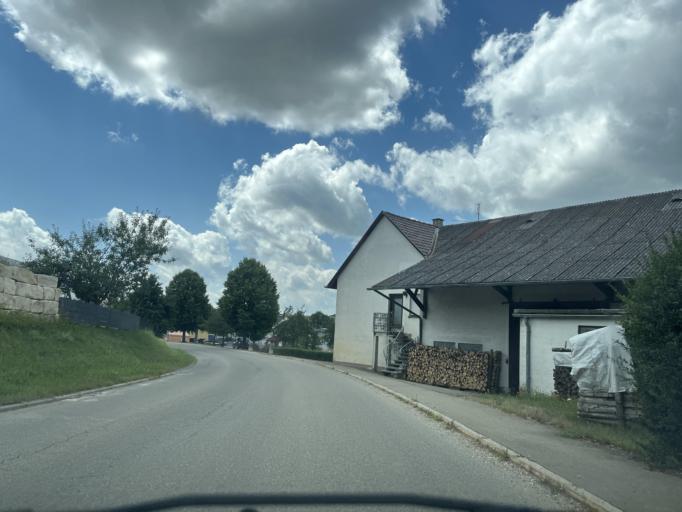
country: DE
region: Baden-Wuerttemberg
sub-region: Tuebingen Region
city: Leibertingen
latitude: 48.0409
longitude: 9.0157
